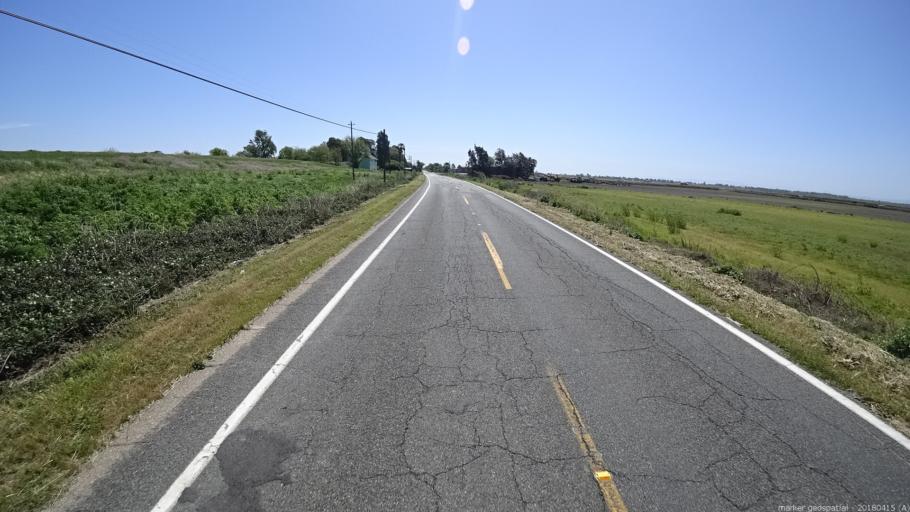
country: US
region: California
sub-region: Solano County
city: Rio Vista
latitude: 38.1361
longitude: -121.5961
